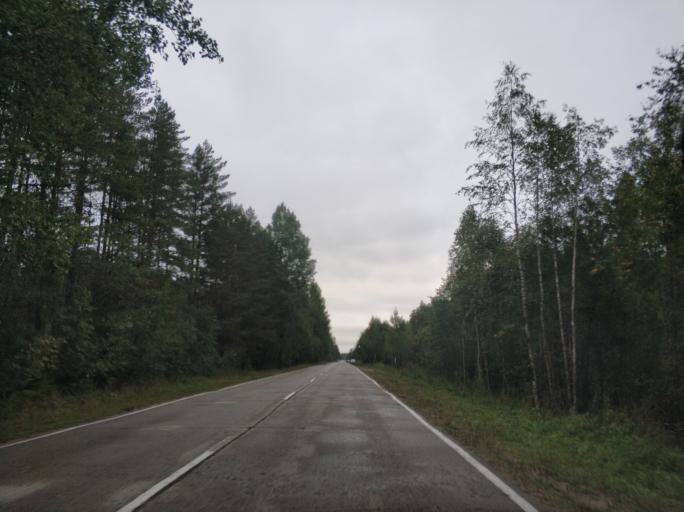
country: RU
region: Leningrad
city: Borisova Griva
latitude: 60.1745
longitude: 30.9194
